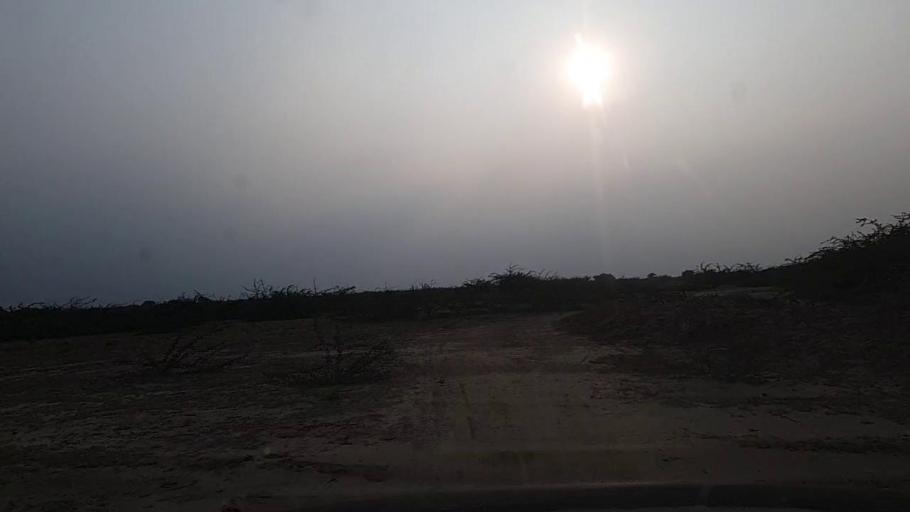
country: PK
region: Sindh
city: Gharo
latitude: 24.7803
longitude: 67.7140
